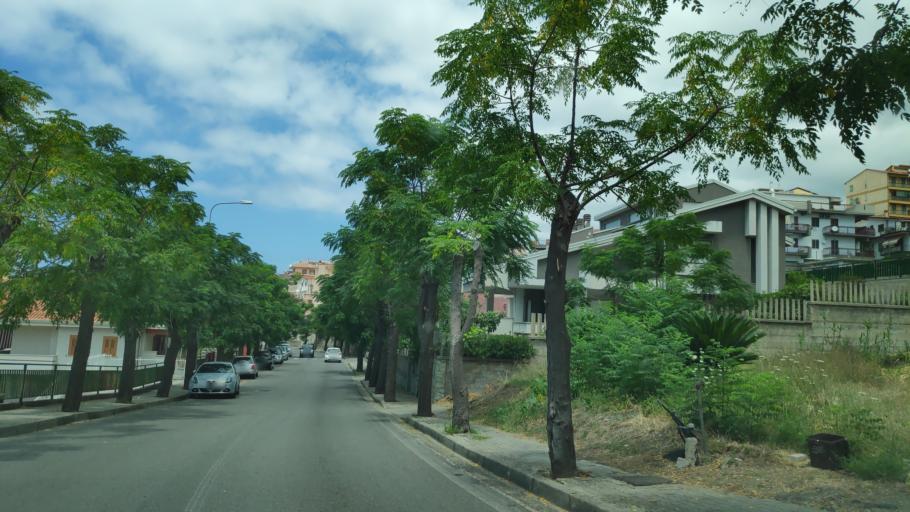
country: IT
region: Calabria
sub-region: Provincia di Cosenza
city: Paola
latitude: 39.3590
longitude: 16.0369
